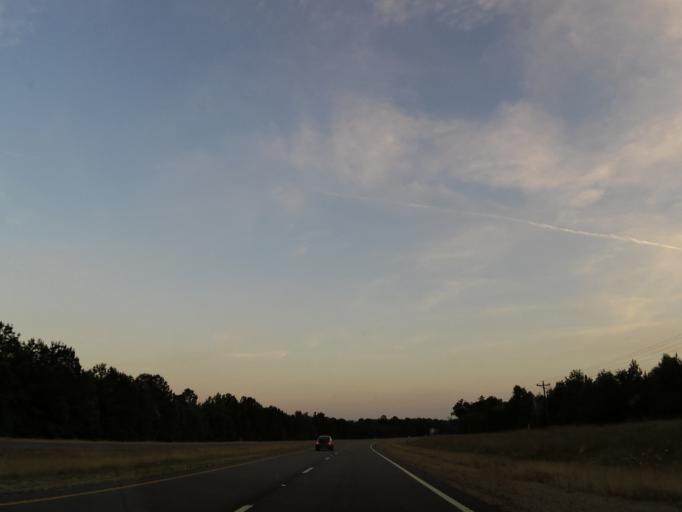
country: US
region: Mississippi
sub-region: Kemper County
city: De Kalb
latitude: 32.8088
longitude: -88.4552
